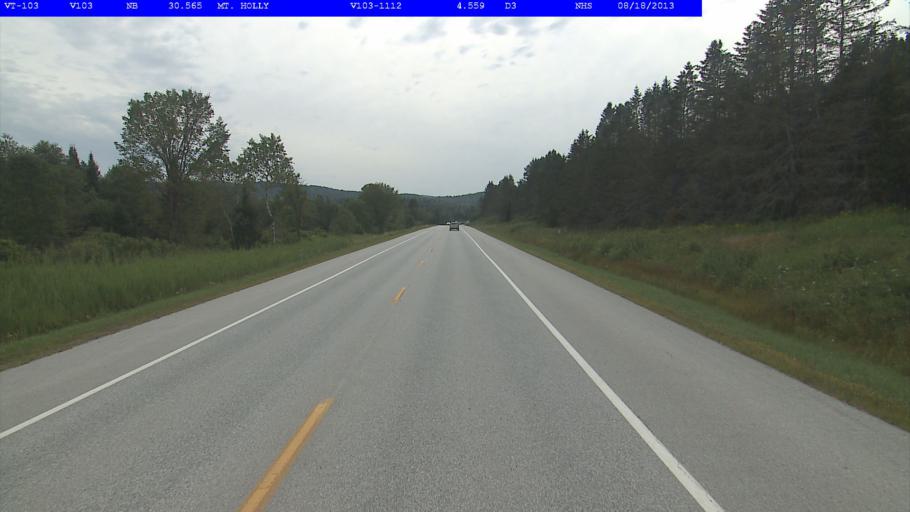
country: US
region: Vermont
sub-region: Rutland County
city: Rutland
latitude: 43.4508
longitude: -72.8128
